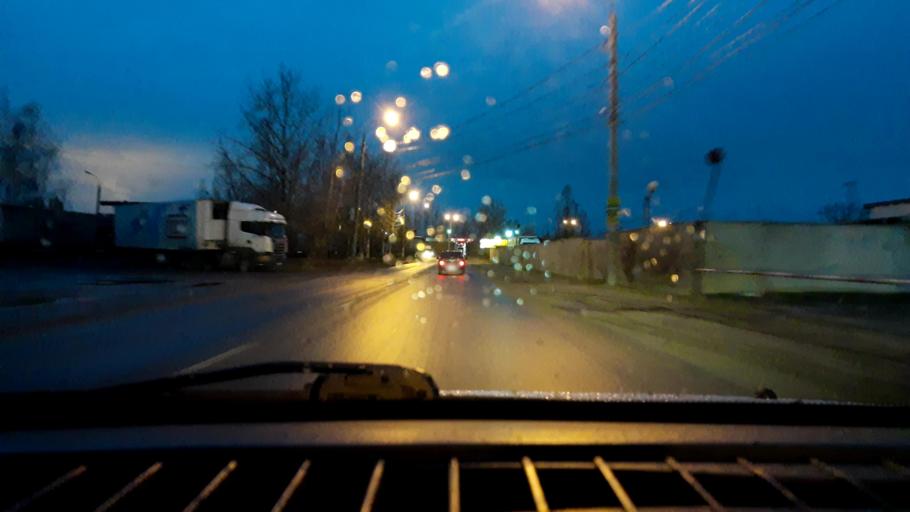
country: RU
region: Nizjnij Novgorod
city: Gorbatovka
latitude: 56.3534
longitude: 43.8032
